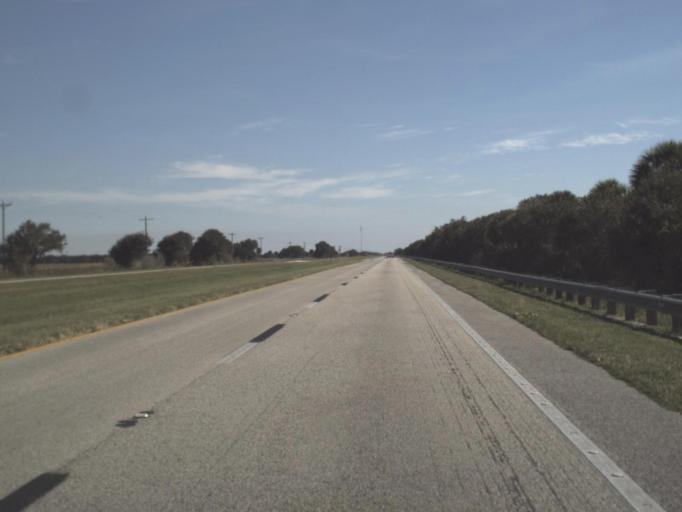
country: US
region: Florida
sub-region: Glades County
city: Moore Haven
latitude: 26.8903
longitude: -81.2352
